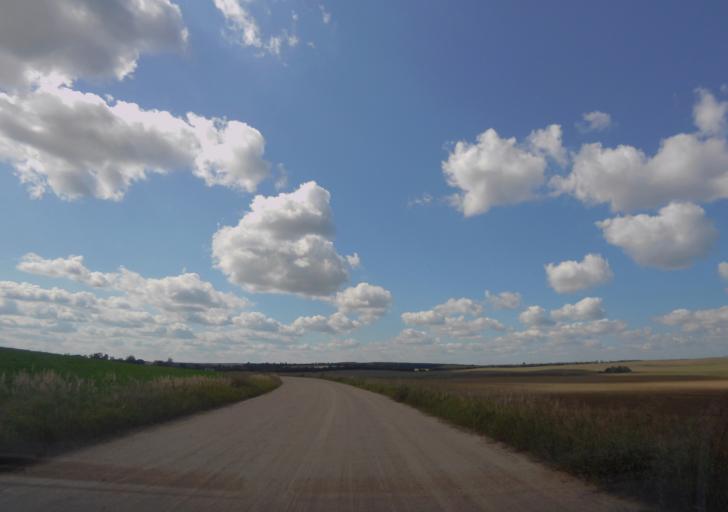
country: BY
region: Minsk
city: Horad Barysaw
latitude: 54.4181
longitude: 28.4616
